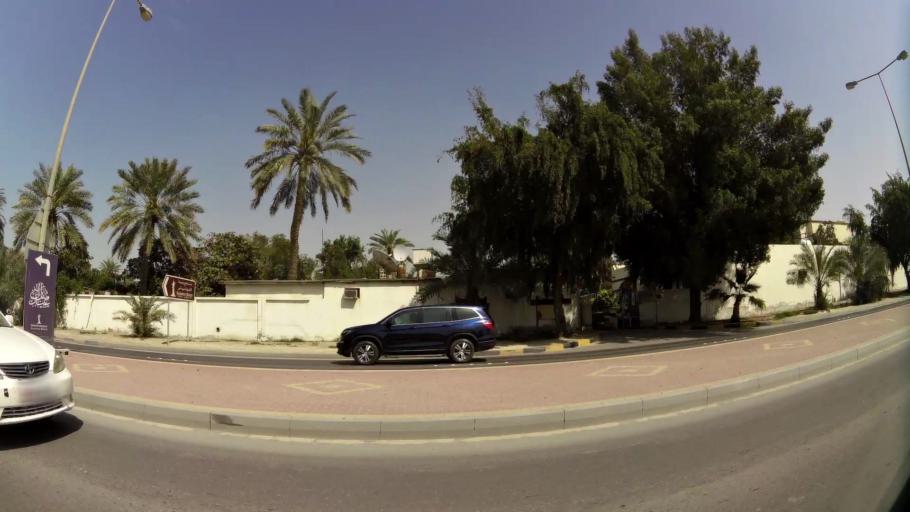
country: BH
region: Manama
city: Jidd Hafs
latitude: 26.2022
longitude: 50.4593
